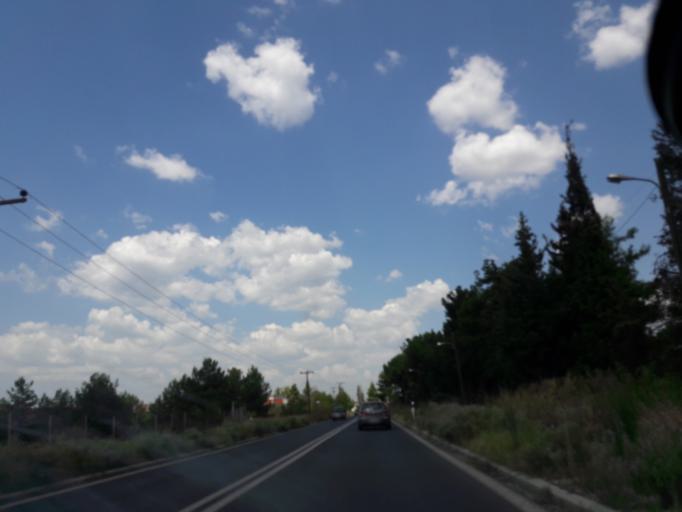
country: GR
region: Central Macedonia
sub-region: Nomos Thessalonikis
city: Thermi
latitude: 40.5363
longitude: 23.0363
